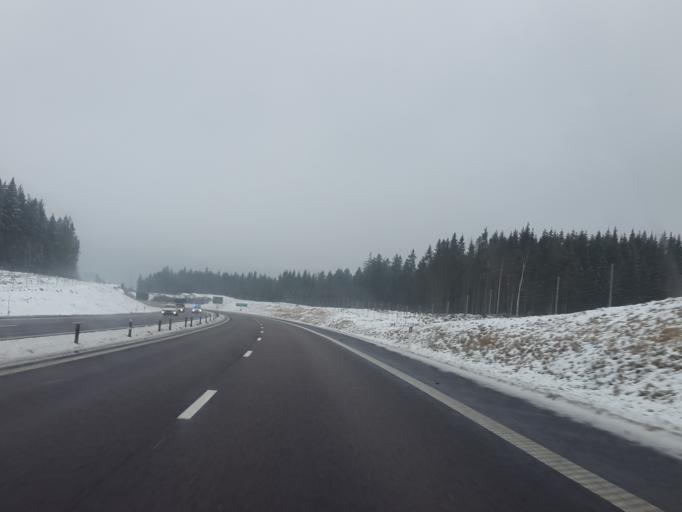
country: SE
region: Vaestra Goetaland
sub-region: Ulricehamns Kommun
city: Ulricehamn
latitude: 57.8096
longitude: 13.4499
